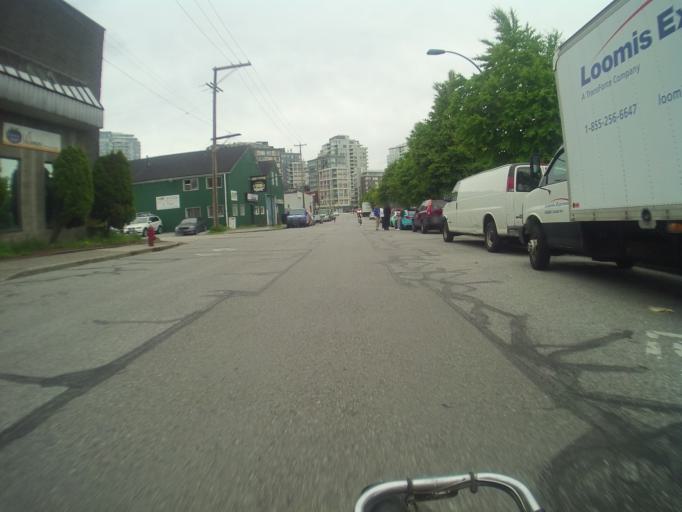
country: CA
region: British Columbia
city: Vancouver
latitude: 49.2691
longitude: -123.0986
